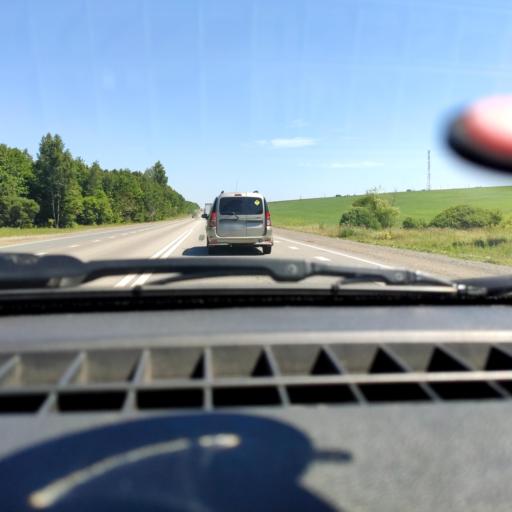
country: RU
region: Bashkortostan
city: Kudeyevskiy
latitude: 54.8001
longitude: 56.6039
